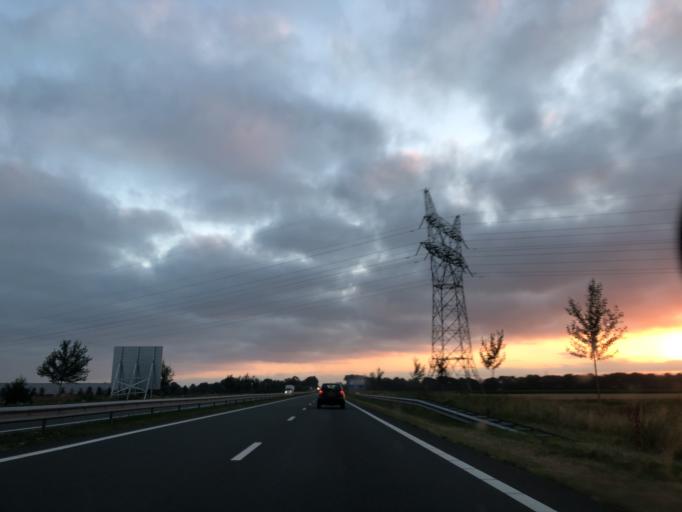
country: NL
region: Groningen
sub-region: Gemeente Veendam
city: Veendam
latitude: 53.0852
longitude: 6.8866
